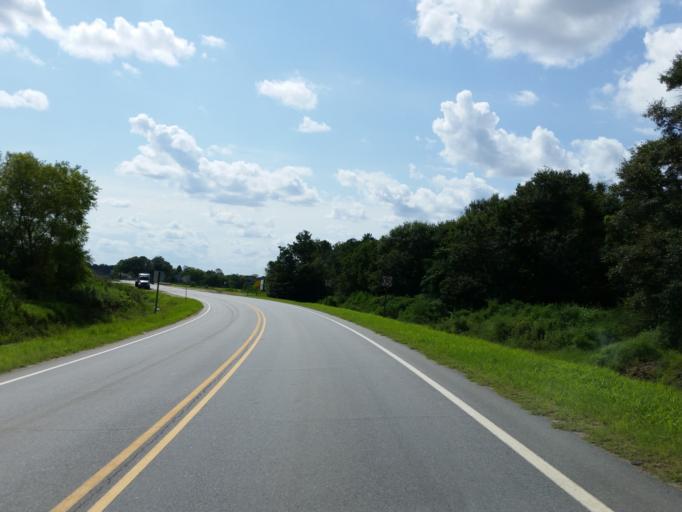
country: US
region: Georgia
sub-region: Turner County
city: Ashburn
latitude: 31.6651
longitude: -83.6042
